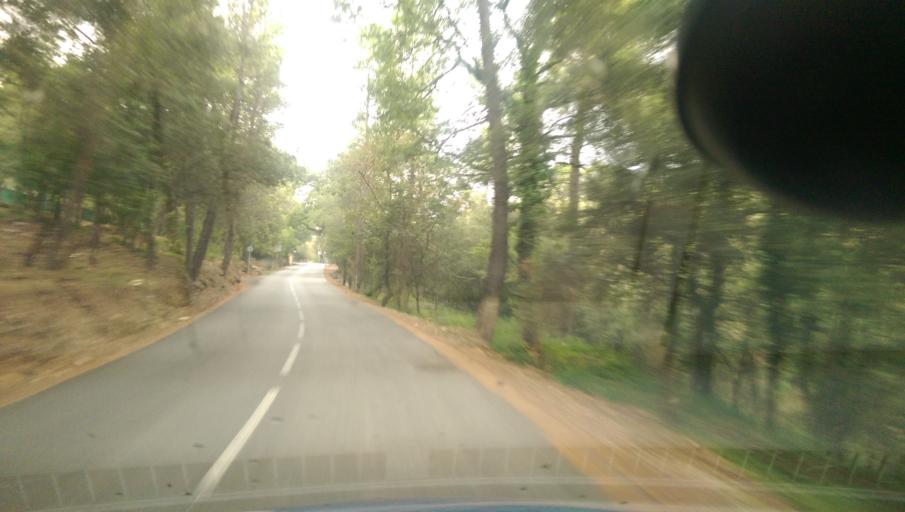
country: FR
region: Provence-Alpes-Cote d'Azur
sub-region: Departement des Alpes-Maritimes
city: Valbonne
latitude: 43.6392
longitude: 7.0407
